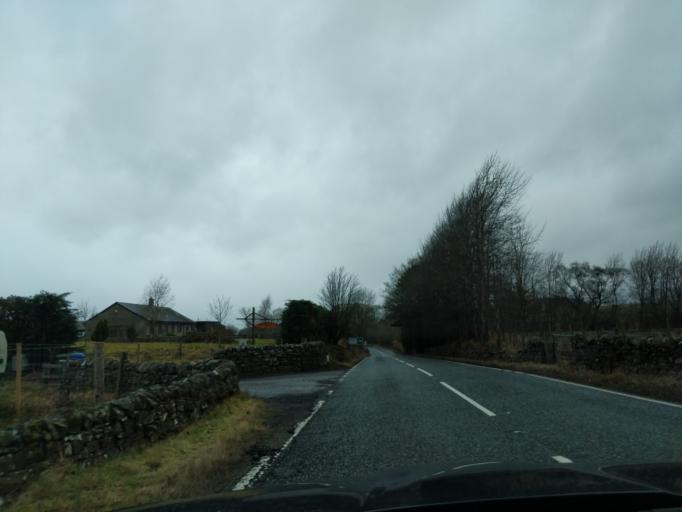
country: GB
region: England
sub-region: Northumberland
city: Otterburn
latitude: 55.2163
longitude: -2.1146
